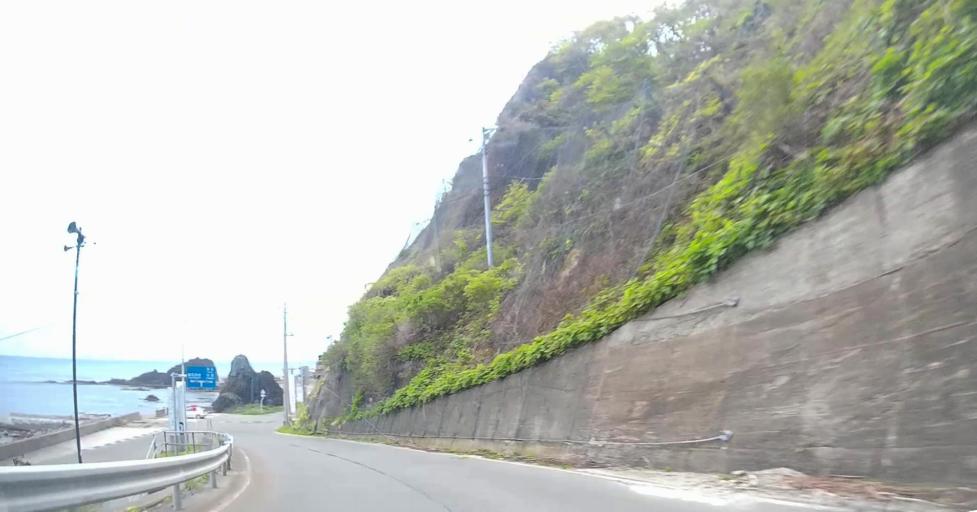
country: JP
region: Aomori
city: Shimokizukuri
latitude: 41.2550
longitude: 140.3522
